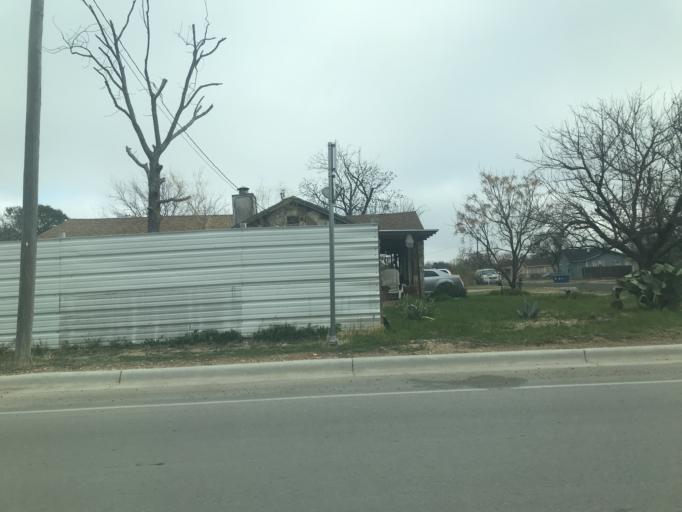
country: US
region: Texas
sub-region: Tom Green County
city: San Angelo
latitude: 31.4769
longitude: -100.4511
